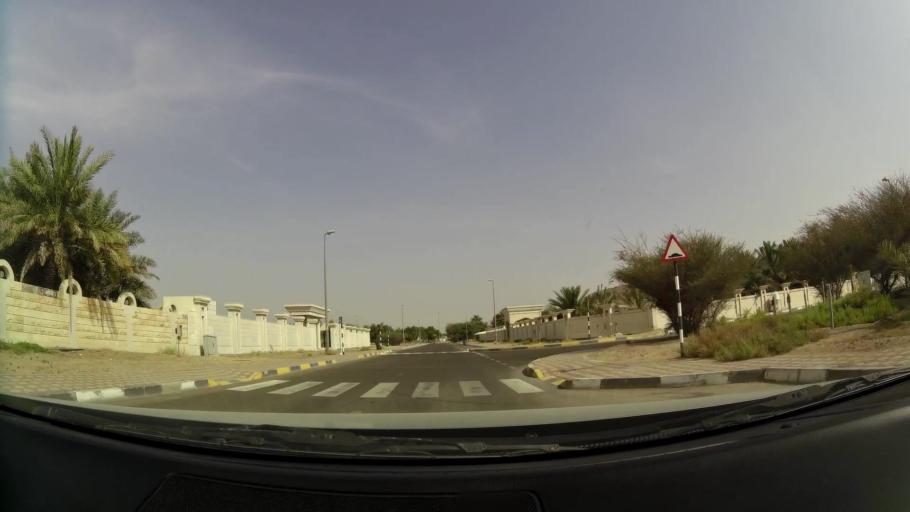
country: AE
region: Abu Dhabi
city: Al Ain
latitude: 24.1607
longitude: 55.7074
